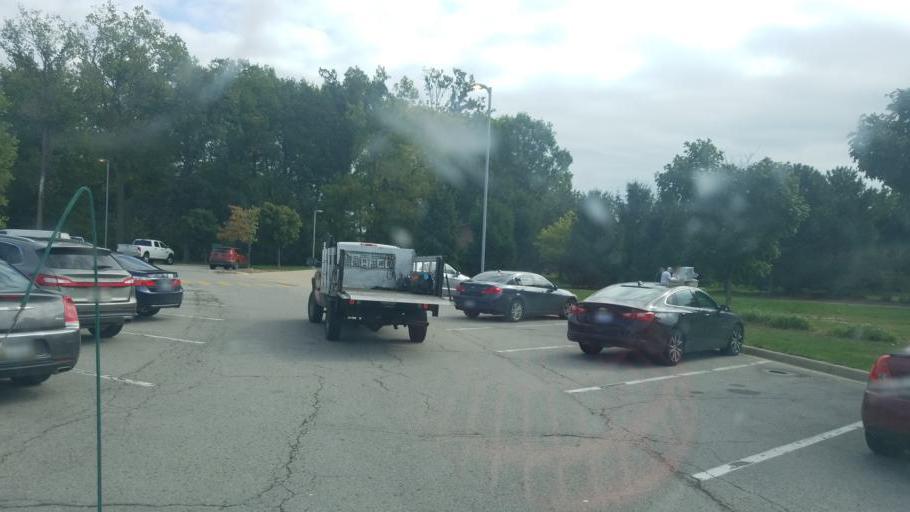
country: US
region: Michigan
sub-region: Monroe County
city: South Monroe
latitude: 41.8632
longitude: -83.4049
